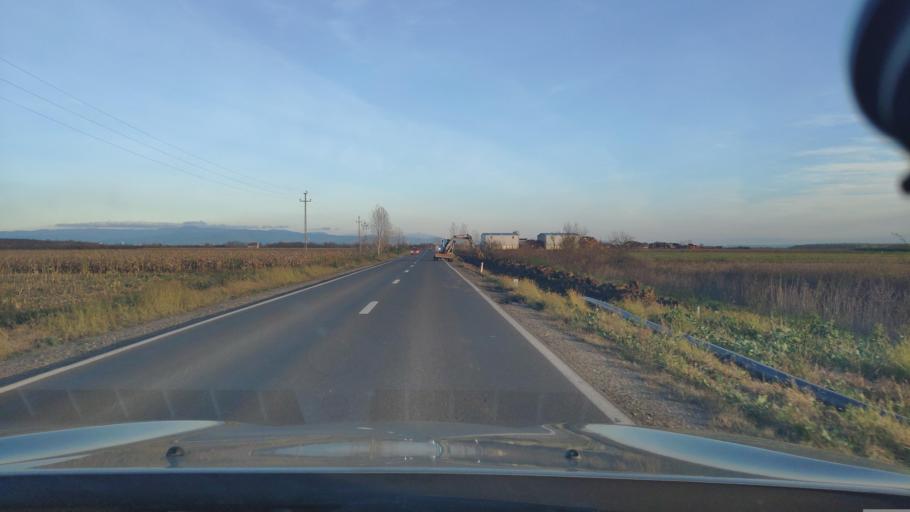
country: RO
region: Satu Mare
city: Culciu Mic
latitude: 47.7818
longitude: 23.0720
